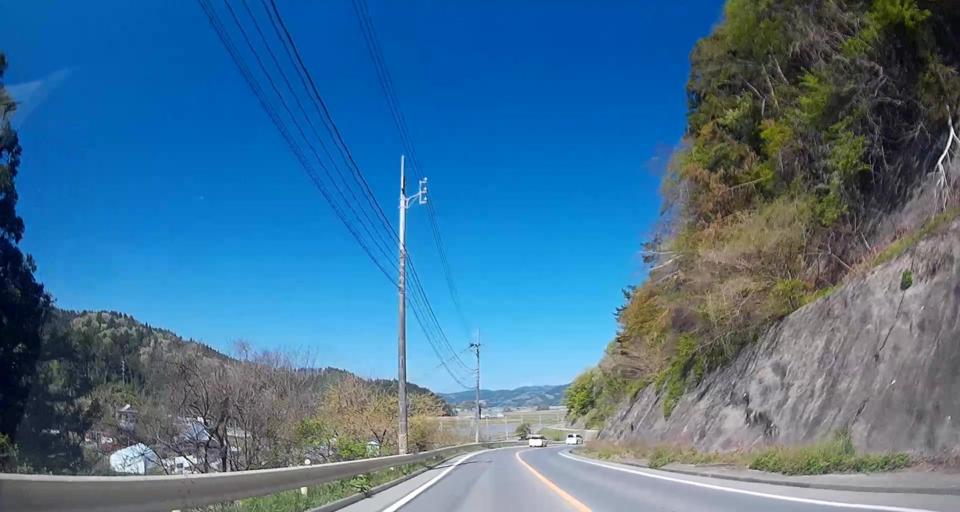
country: JP
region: Miyagi
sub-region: Oshika Gun
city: Onagawa Cho
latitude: 38.5353
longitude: 141.4365
